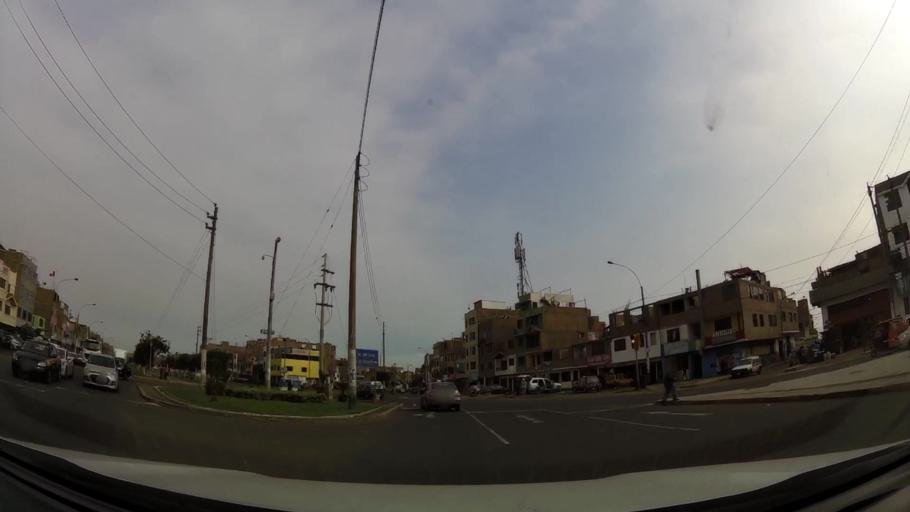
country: PE
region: Callao
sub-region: Callao
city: Callao
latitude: -12.0242
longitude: -77.0990
